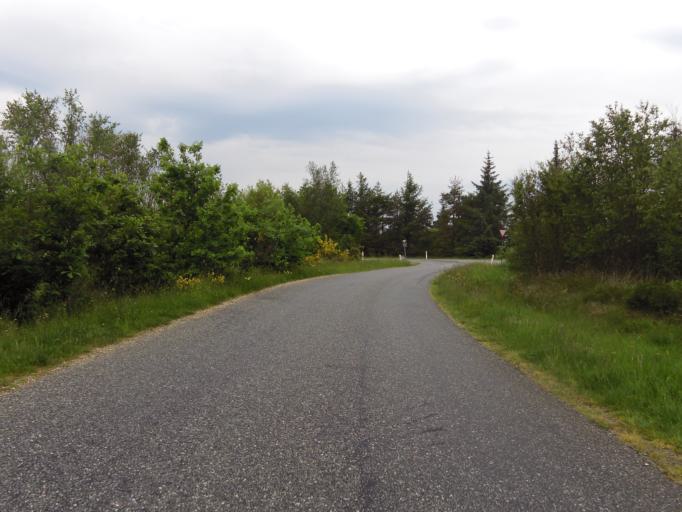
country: DK
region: South Denmark
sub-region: Esbjerg Kommune
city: Ribe
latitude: 55.3033
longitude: 8.8763
